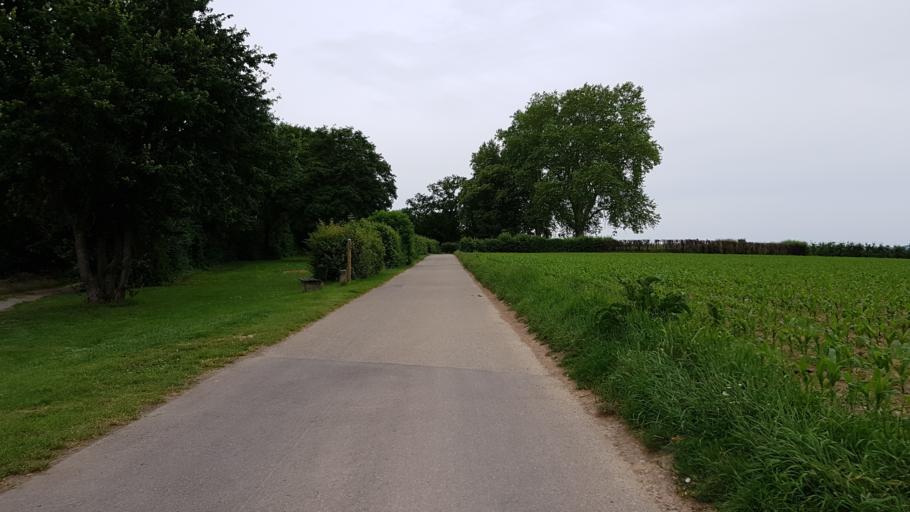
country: DE
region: Baden-Wuerttemberg
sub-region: Regierungsbezirk Stuttgart
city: Marbach am Neckar
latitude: 48.9492
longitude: 9.2691
